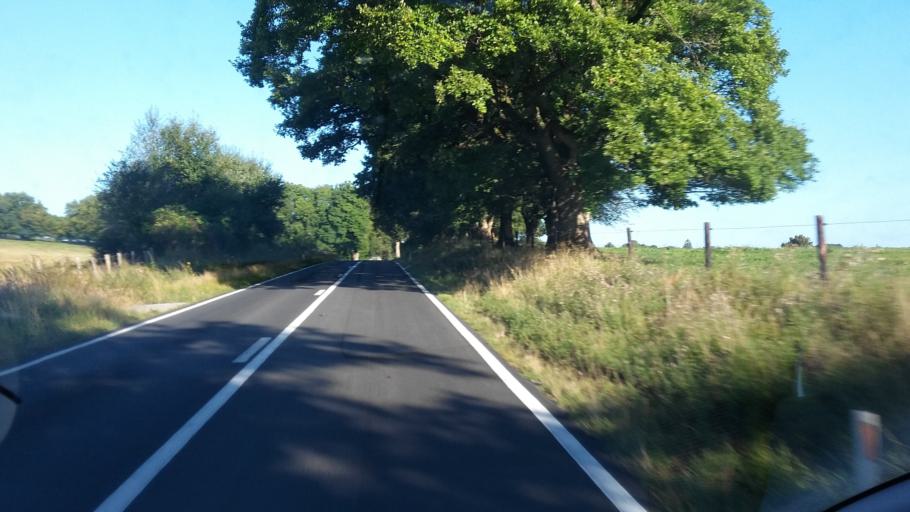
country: BE
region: Wallonia
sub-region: Province du Luxembourg
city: Leglise
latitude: 49.8187
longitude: 5.4967
